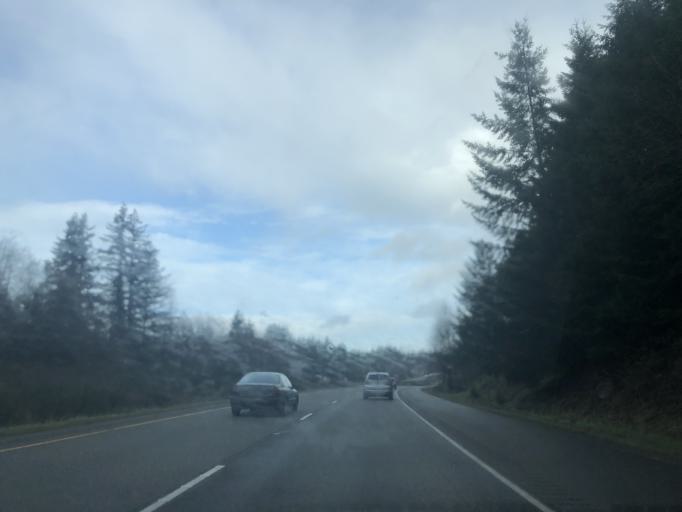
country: US
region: Washington
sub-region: Kitsap County
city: Silverdale
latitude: 47.6487
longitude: -122.7062
